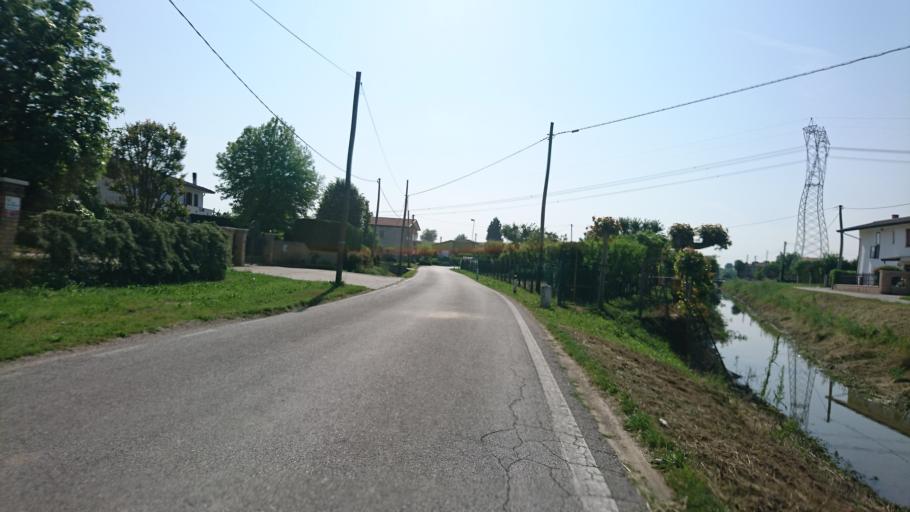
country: IT
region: Veneto
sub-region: Provincia di Venezia
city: Galta
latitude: 45.3671
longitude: 12.0295
